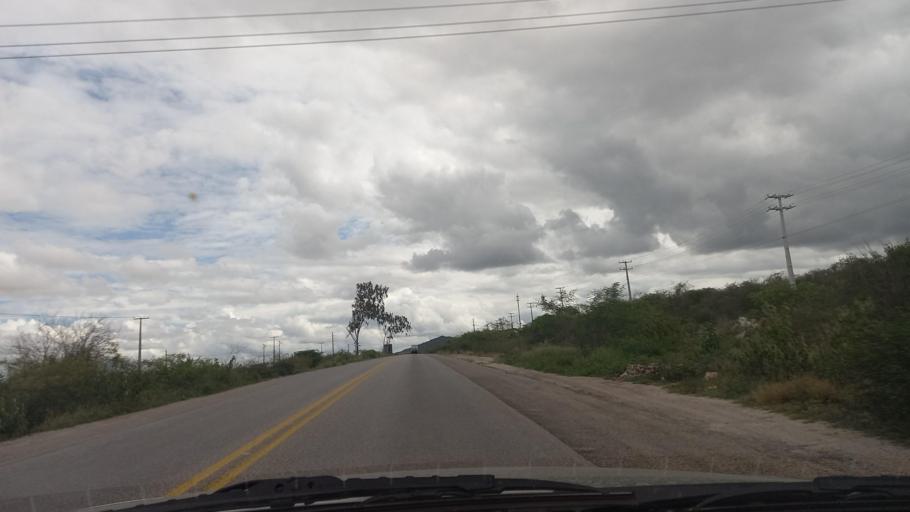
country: BR
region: Pernambuco
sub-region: Cachoeirinha
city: Cachoeirinha
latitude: -8.3330
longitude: -36.1510
